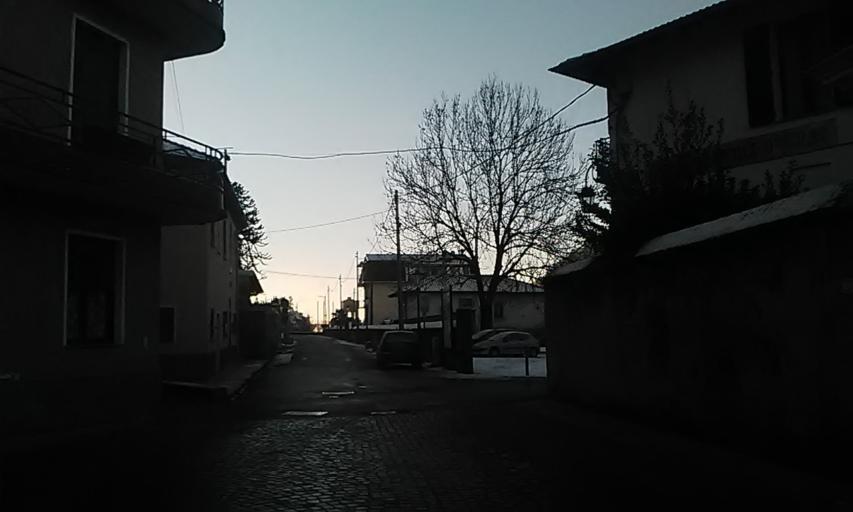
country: IT
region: Piedmont
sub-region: Provincia di Novara
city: Prato Sesia
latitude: 45.6437
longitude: 8.3761
